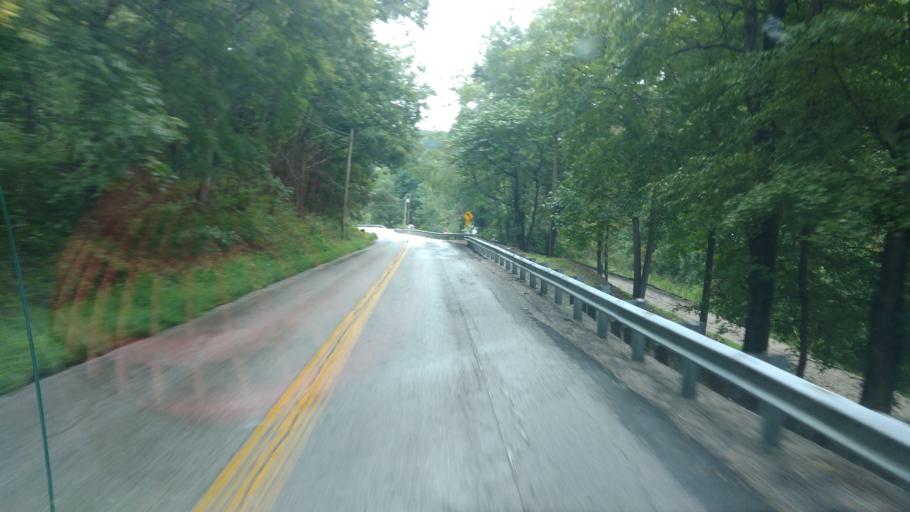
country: US
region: Kentucky
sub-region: Fleming County
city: Flemingsburg
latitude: 38.4514
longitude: -83.5203
